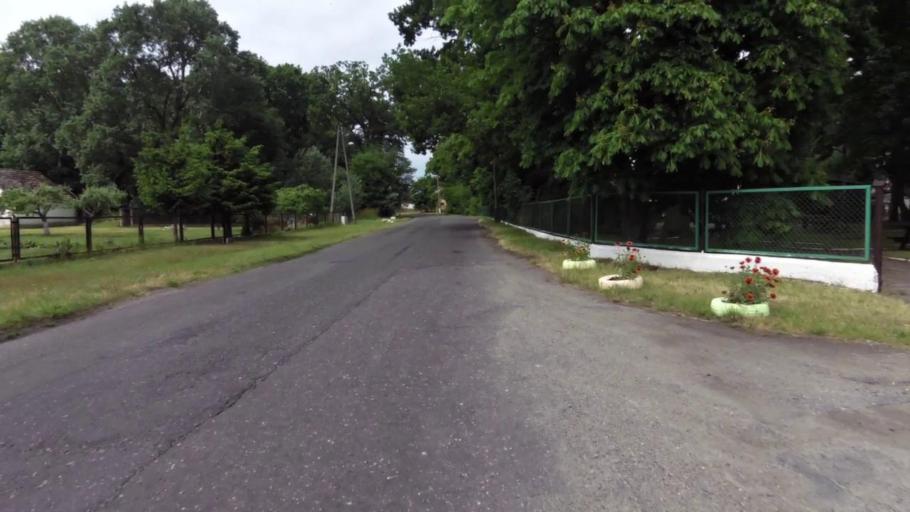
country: PL
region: West Pomeranian Voivodeship
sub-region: Powiat goleniowski
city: Stepnica
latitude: 53.7193
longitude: 14.5550
